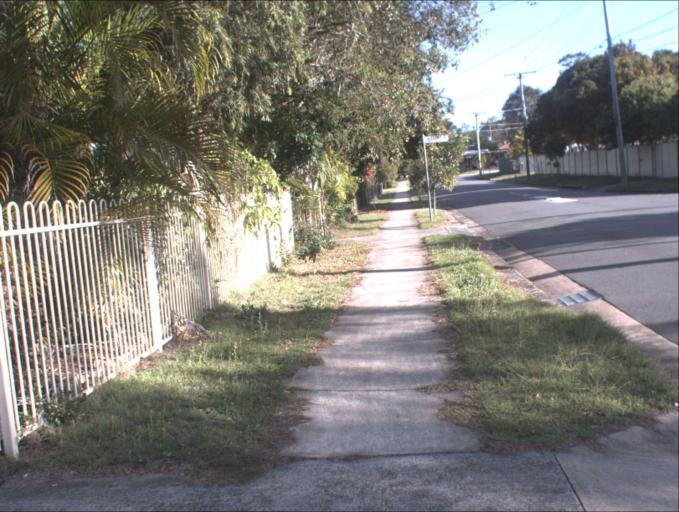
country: AU
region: Queensland
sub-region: Logan
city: Waterford West
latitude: -27.6771
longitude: 153.1045
